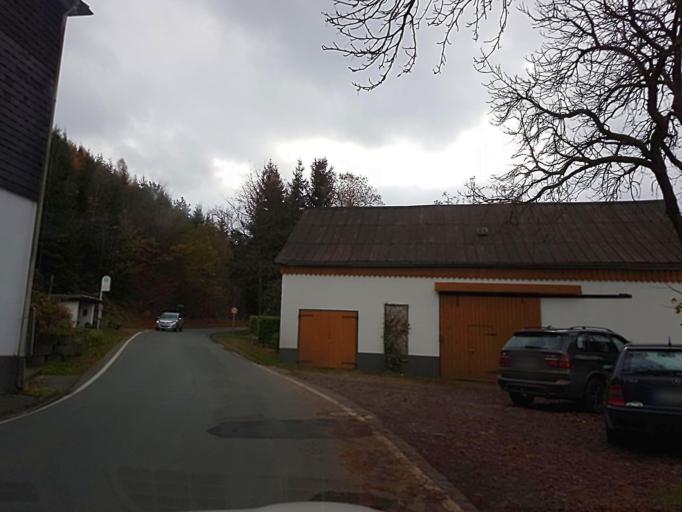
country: DE
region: North Rhine-Westphalia
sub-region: Regierungsbezirk Arnsberg
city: Drolshagen
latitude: 51.0633
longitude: 7.7694
